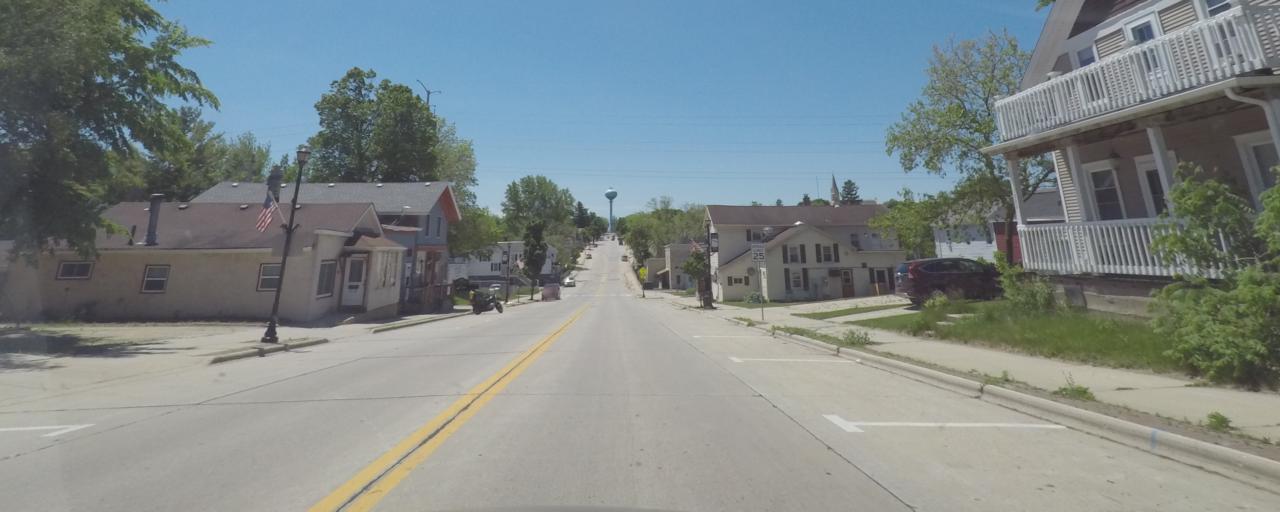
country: US
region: Wisconsin
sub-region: Washington County
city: West Bend
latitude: 43.4430
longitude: -88.1798
